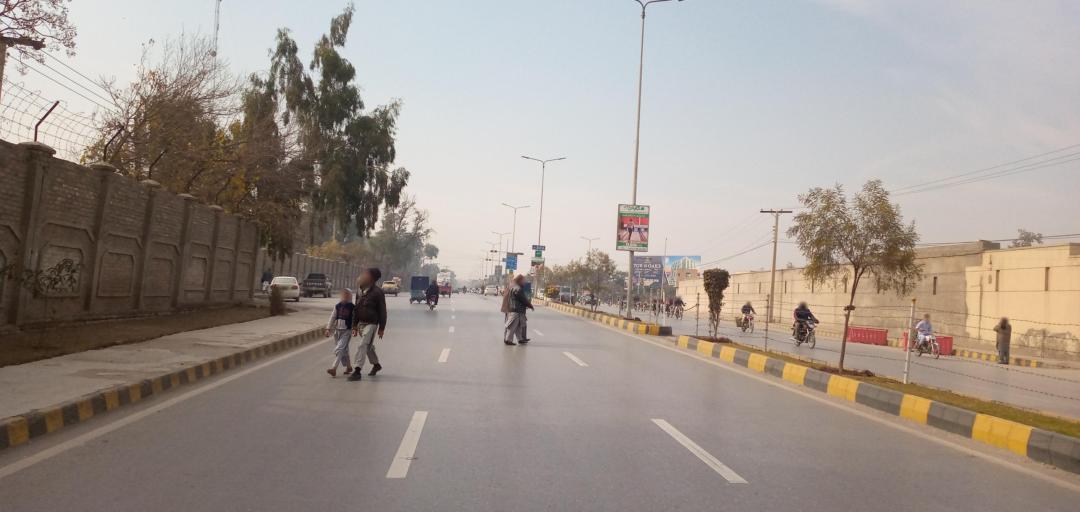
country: PK
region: Khyber Pakhtunkhwa
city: Peshawar
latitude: 34.0145
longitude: 71.5536
